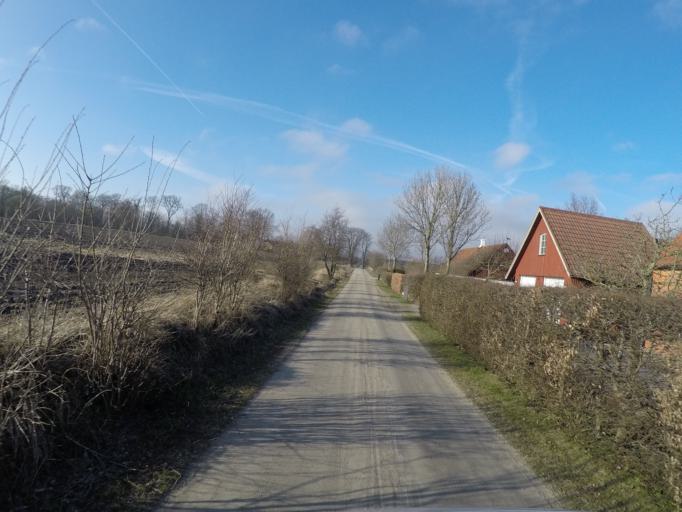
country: SE
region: Skane
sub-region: Lunds Kommun
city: Lund
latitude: 55.6943
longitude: 13.2713
